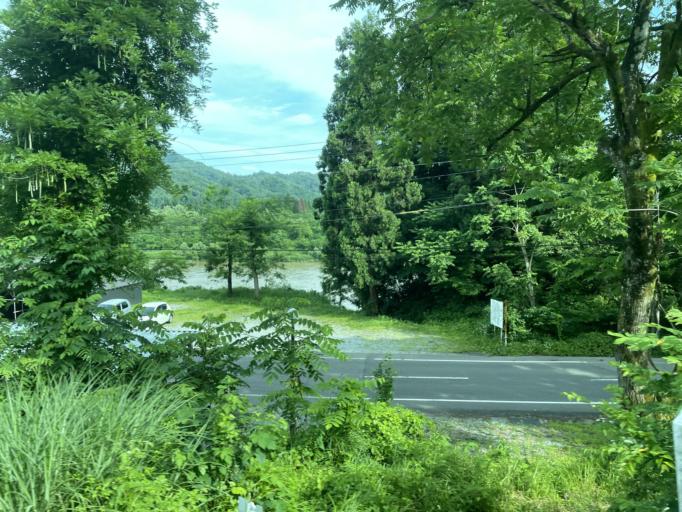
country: JP
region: Niigata
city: Suibara
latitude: 37.6949
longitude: 139.4767
